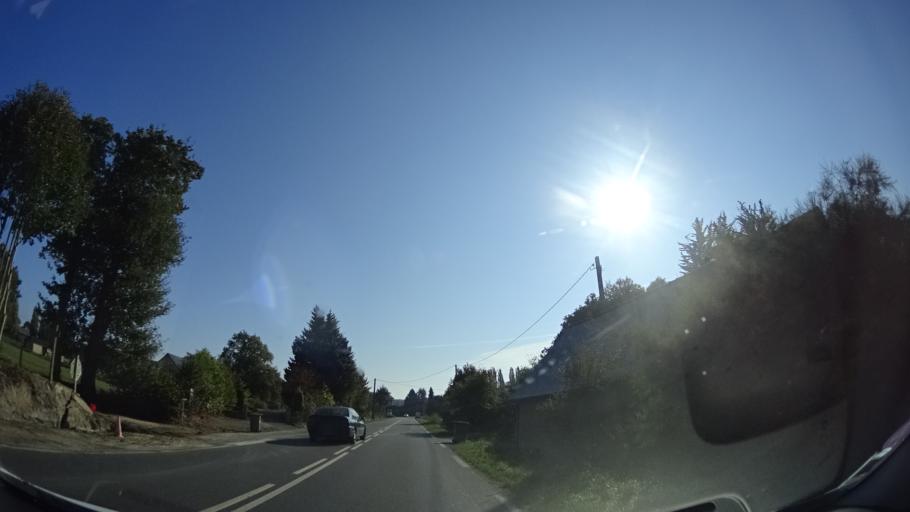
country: FR
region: Brittany
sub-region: Departement d'Ille-et-Vilaine
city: Geveze
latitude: 48.2139
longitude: -1.7725
